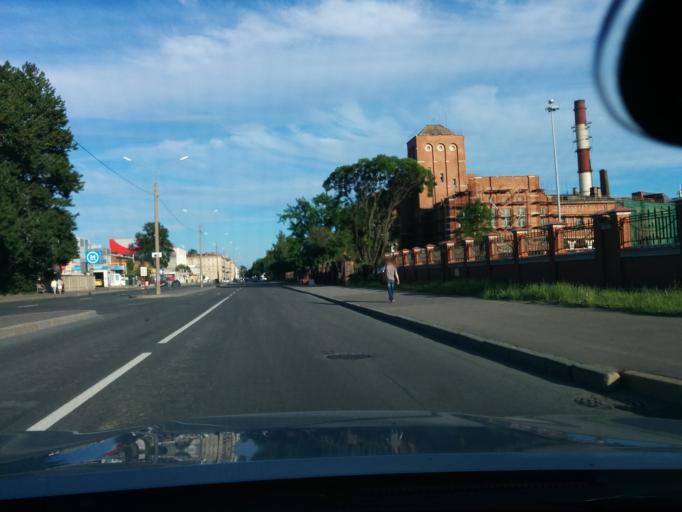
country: RU
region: Leningrad
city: Finlyandskiy
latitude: 59.9741
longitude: 30.3772
